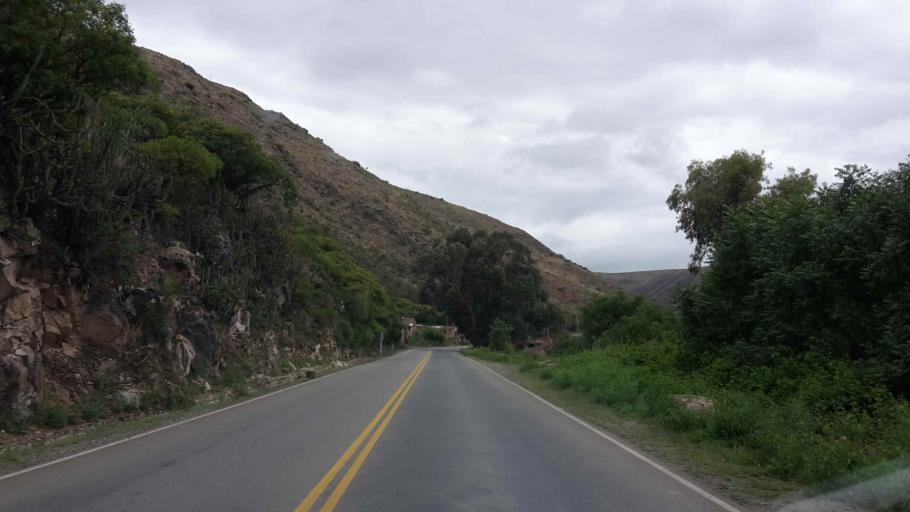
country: BO
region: Cochabamba
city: Punata
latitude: -17.5126
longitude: -65.8116
